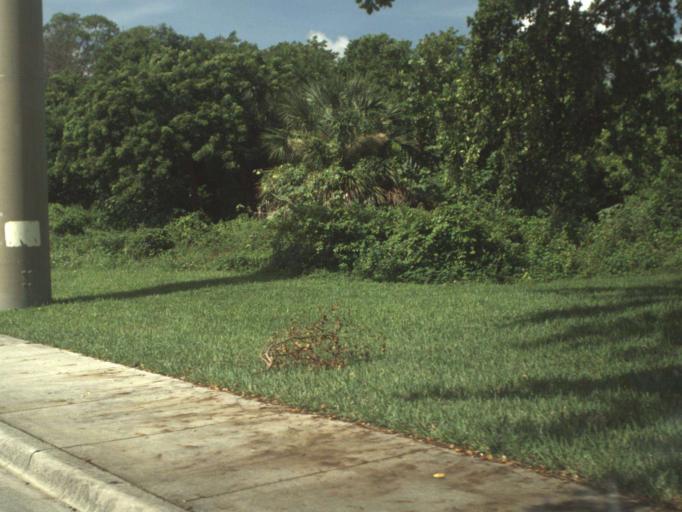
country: US
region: Florida
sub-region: Miami-Dade County
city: North Miami Beach
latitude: 25.9341
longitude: -80.1513
